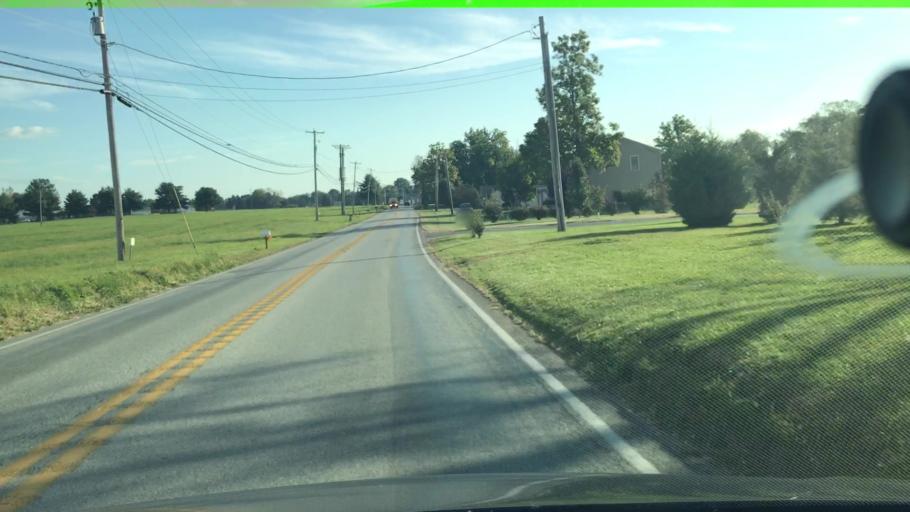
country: US
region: Pennsylvania
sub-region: York County
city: Weigelstown
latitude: 40.0222
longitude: -76.8041
